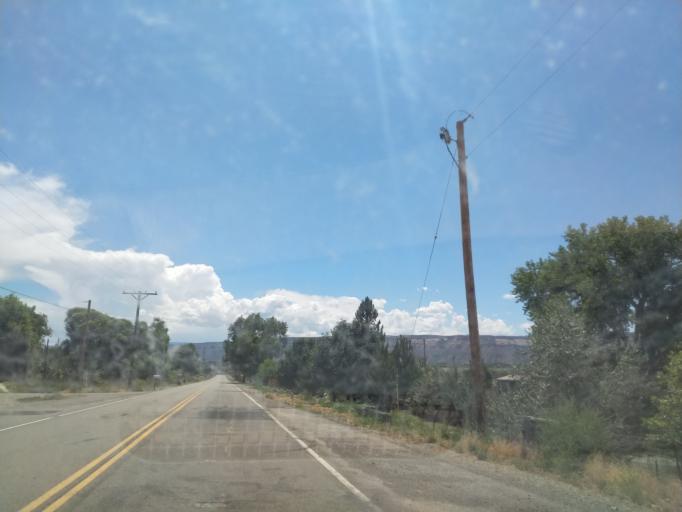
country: US
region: Colorado
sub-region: Mesa County
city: Redlands
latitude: 39.1255
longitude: -108.6639
